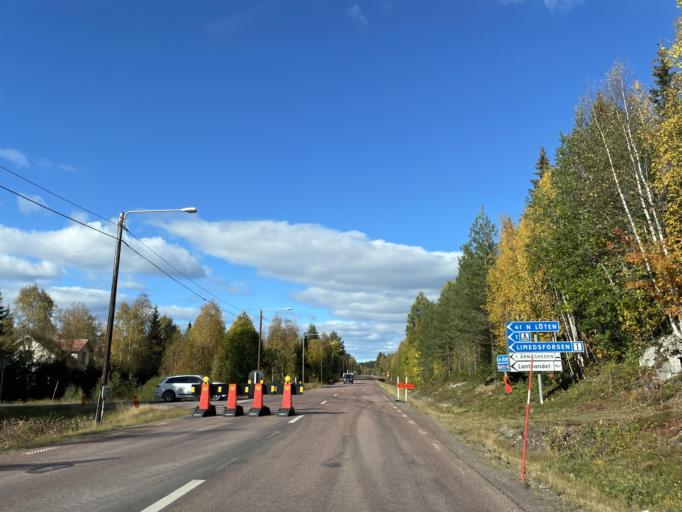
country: SE
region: Dalarna
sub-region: Malung-Saelens kommun
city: Malung
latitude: 60.9041
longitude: 13.3842
